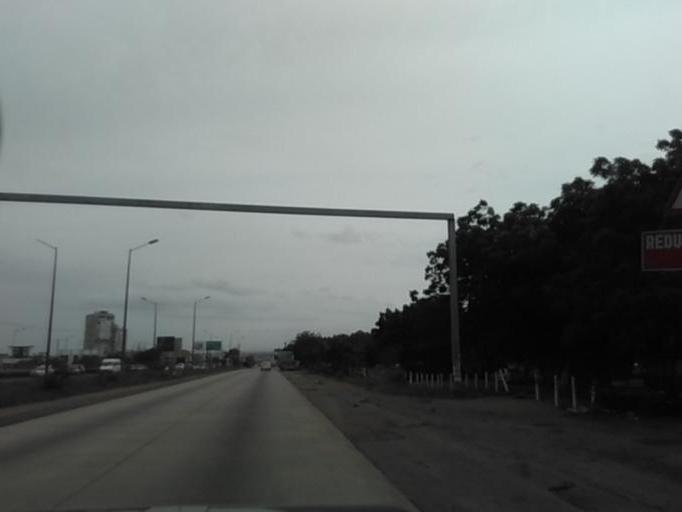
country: GH
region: Greater Accra
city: Medina Estates
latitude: 5.6252
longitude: -0.1704
